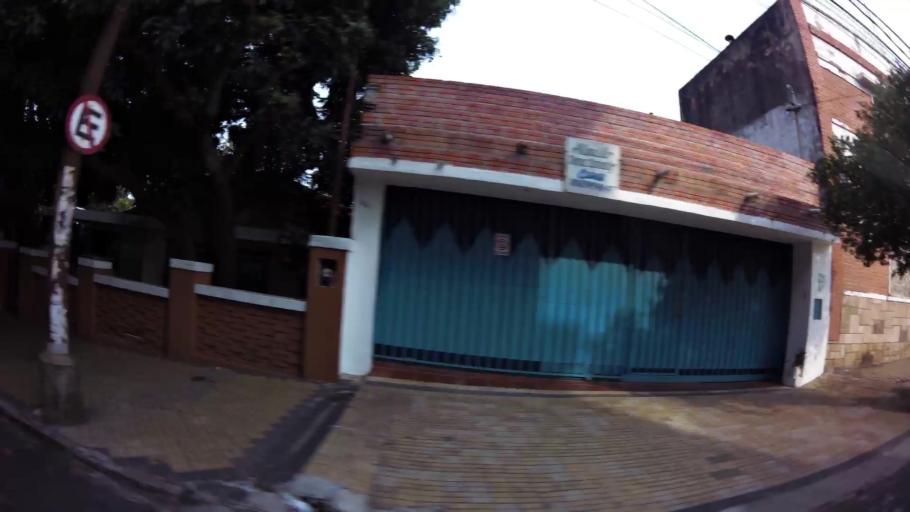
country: PY
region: Asuncion
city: Asuncion
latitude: -25.2981
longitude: -57.6178
